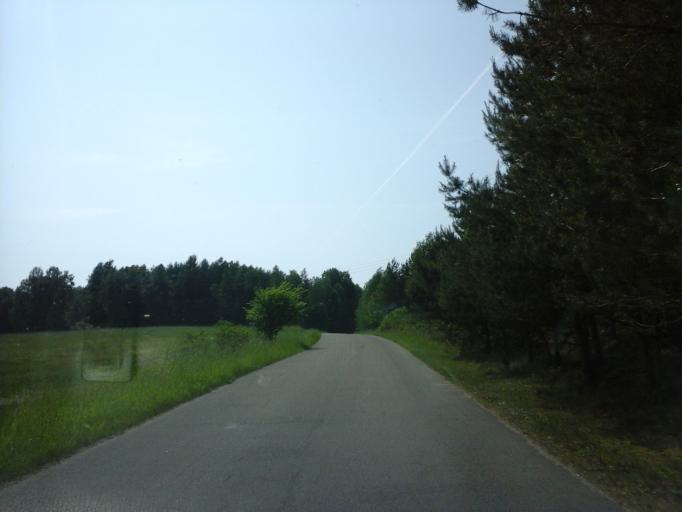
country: PL
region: West Pomeranian Voivodeship
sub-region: Powiat stargardzki
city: Insko
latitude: 53.3606
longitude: 15.5361
